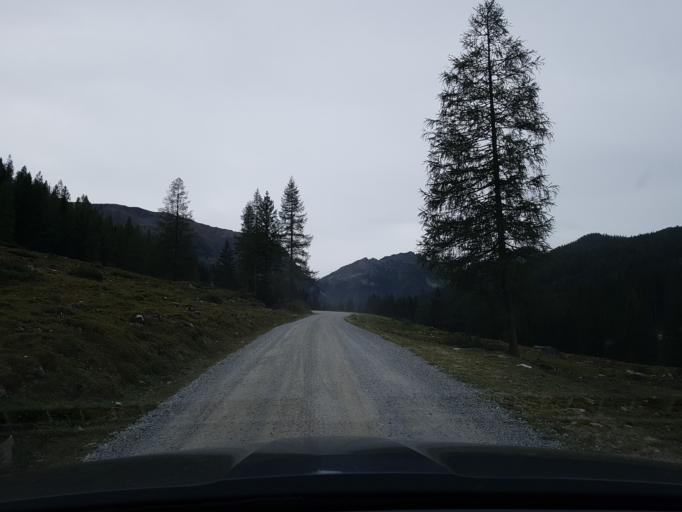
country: AT
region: Salzburg
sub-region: Politischer Bezirk Sankt Johann im Pongau
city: Forstau
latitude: 47.3059
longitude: 13.5823
